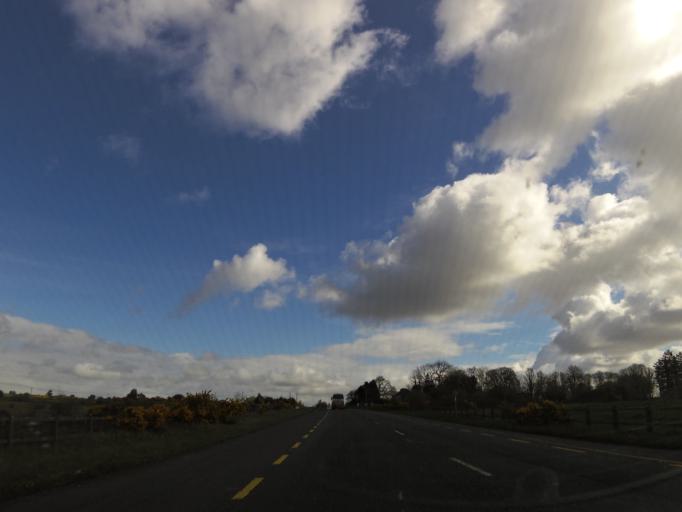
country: IE
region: Connaught
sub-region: Maigh Eo
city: Ballyhaunis
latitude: 53.8348
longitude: -8.8621
